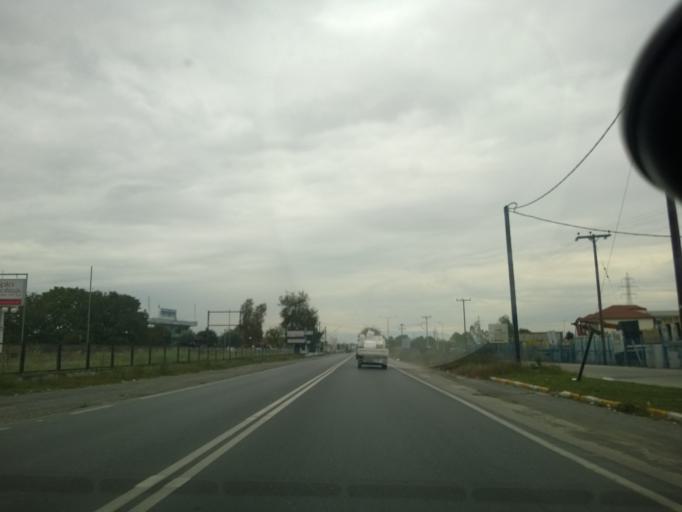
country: GR
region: Central Macedonia
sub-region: Nomos Pellis
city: Melissi
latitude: 40.7806
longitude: 22.3770
